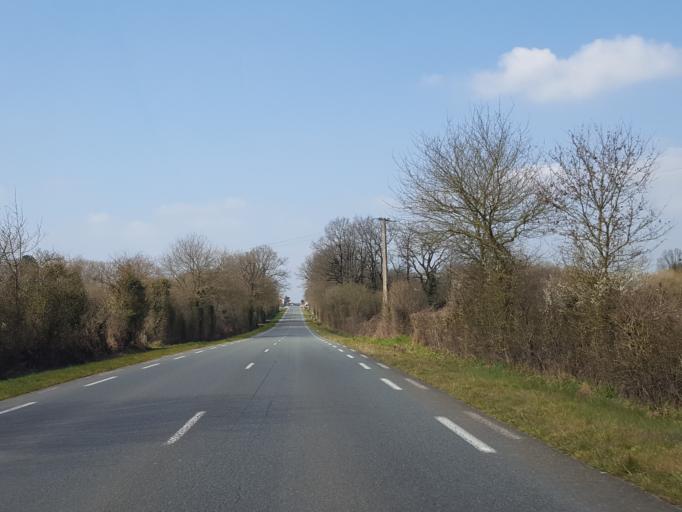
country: FR
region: Pays de la Loire
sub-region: Departement de la Vendee
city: La Chaize-le-Vicomte
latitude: 46.6670
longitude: -1.2791
